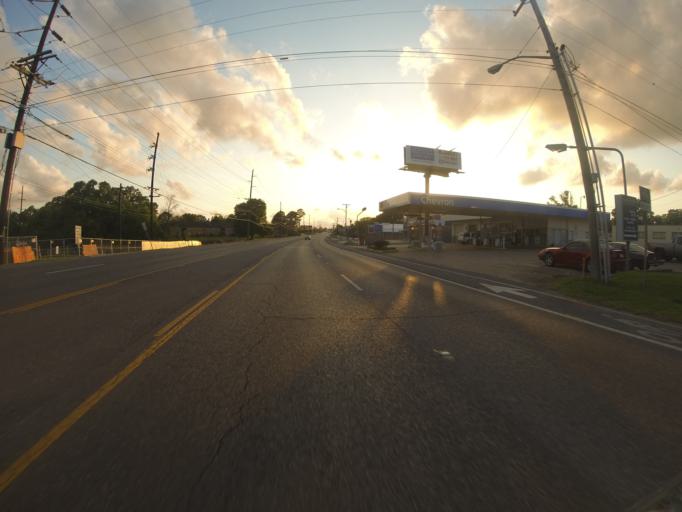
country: US
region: Louisiana
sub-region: Lafayette Parish
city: Lafayette
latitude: 30.2053
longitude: -92.0421
